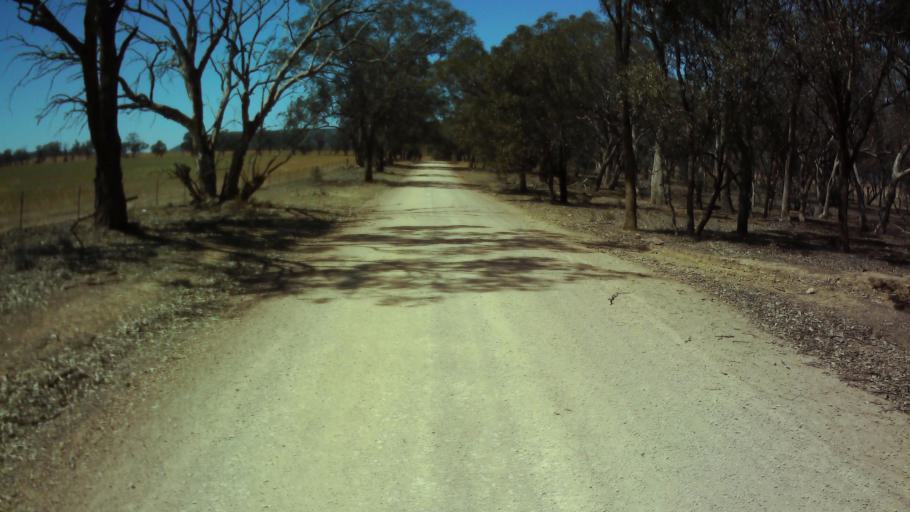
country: AU
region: New South Wales
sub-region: Weddin
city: Grenfell
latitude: -33.9262
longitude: 148.0782
